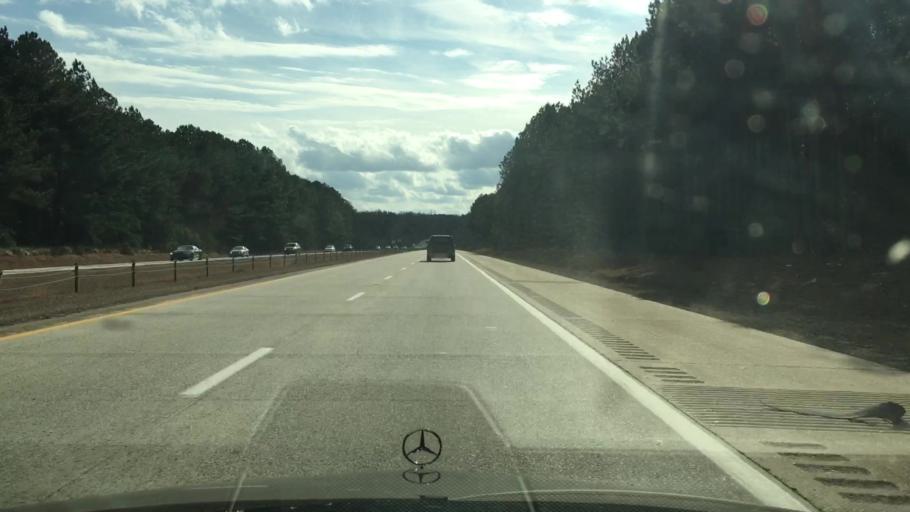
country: US
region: North Carolina
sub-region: Johnston County
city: Clayton
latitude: 35.5708
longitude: -78.5764
